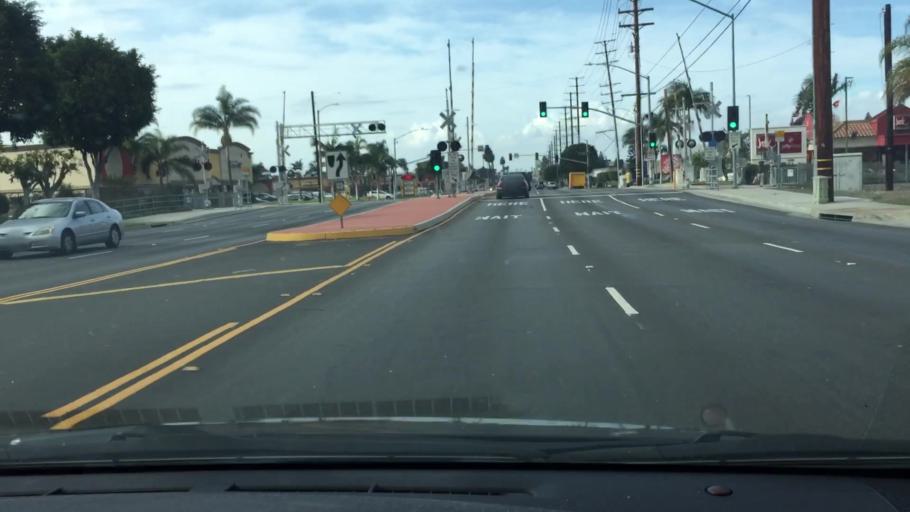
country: US
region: California
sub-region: Orange County
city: Orange
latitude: 33.8091
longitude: -117.8555
